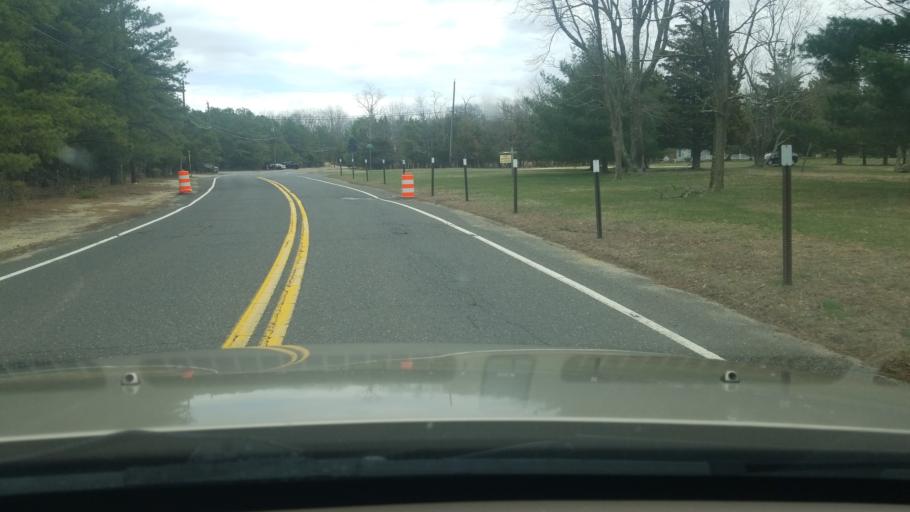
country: US
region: New Jersey
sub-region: Monmouth County
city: Ramtown
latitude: 40.1340
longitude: -74.1239
